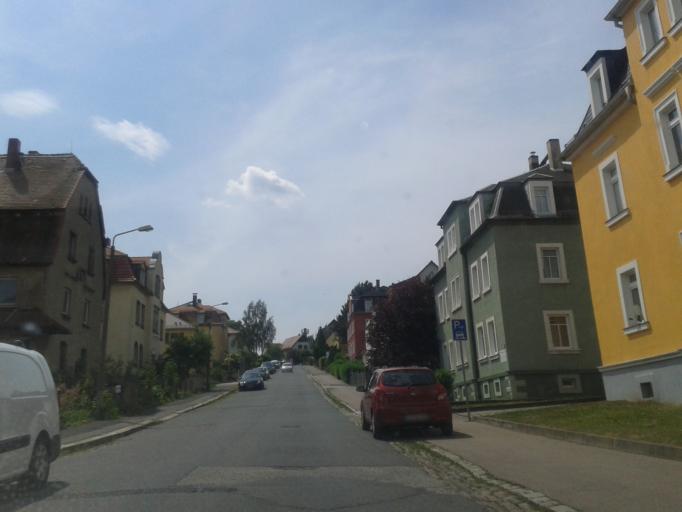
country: DE
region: Saxony
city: Bannewitz
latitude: 50.9972
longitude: 13.7236
